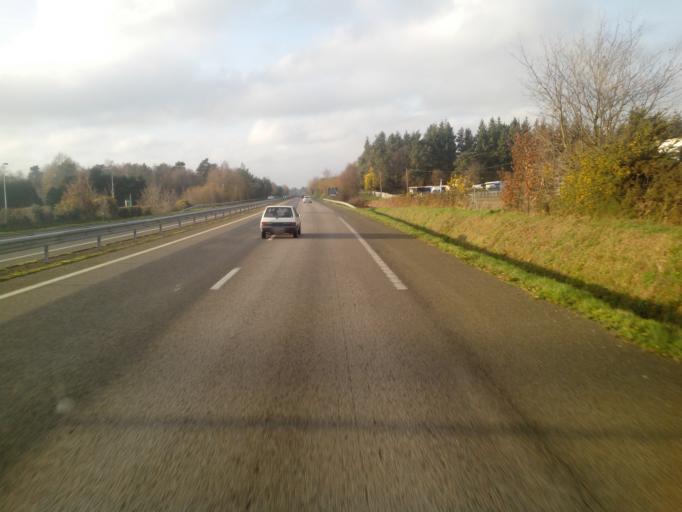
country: FR
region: Brittany
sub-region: Departement du Morbihan
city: Guillac
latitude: 47.9413
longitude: -2.5006
